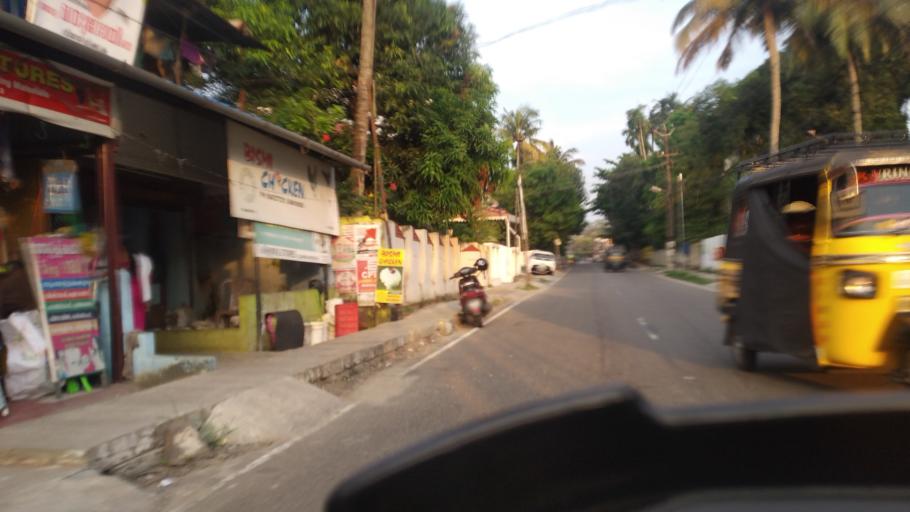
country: IN
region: Kerala
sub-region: Ernakulam
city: Elur
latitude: 10.0190
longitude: 76.2877
